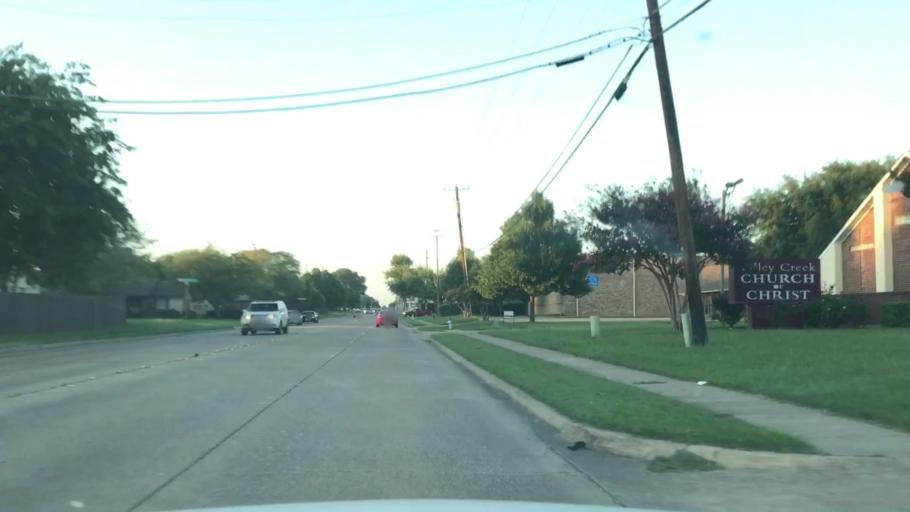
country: US
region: Texas
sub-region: Dallas County
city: Mesquite
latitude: 32.7475
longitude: -96.5834
